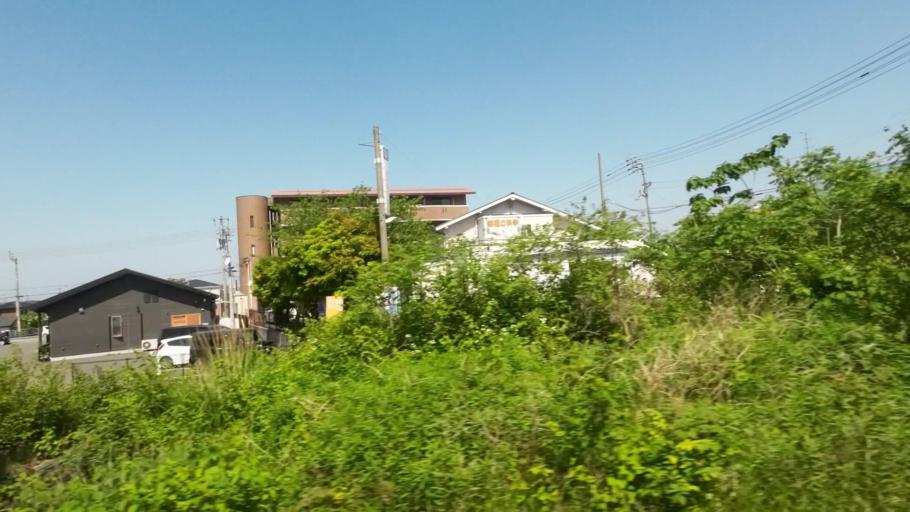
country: JP
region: Ehime
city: Niihama
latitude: 33.9540
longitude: 133.3015
